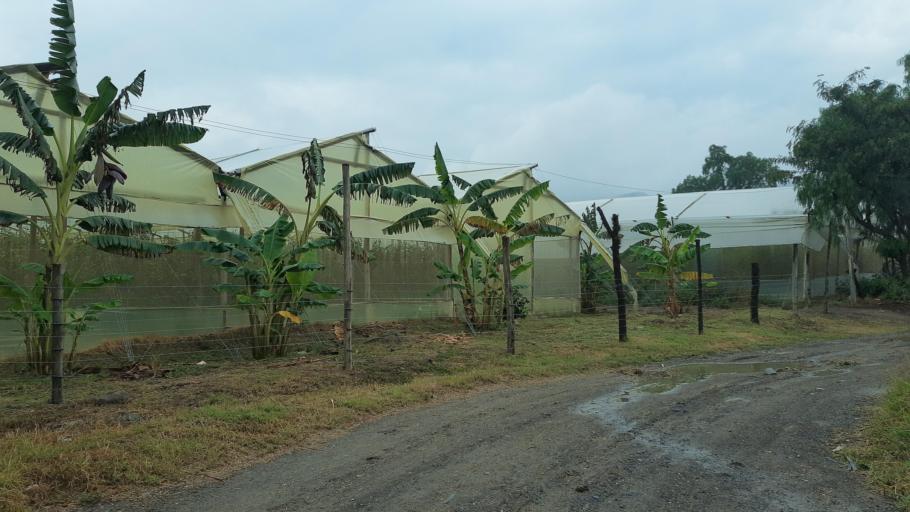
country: CO
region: Boyaca
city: Sachica
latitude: 5.5894
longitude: -73.5468
